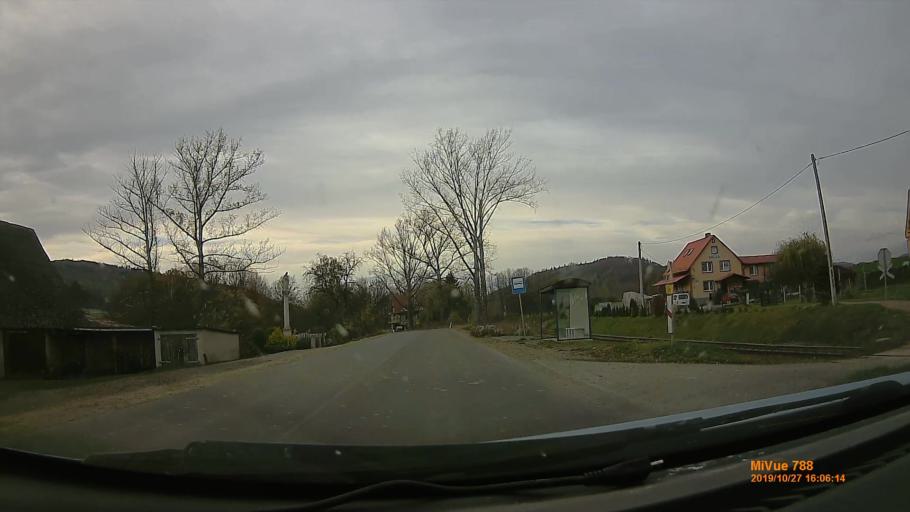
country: PL
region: Lower Silesian Voivodeship
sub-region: Powiat klodzki
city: Nowa Ruda
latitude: 50.5378
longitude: 16.4752
